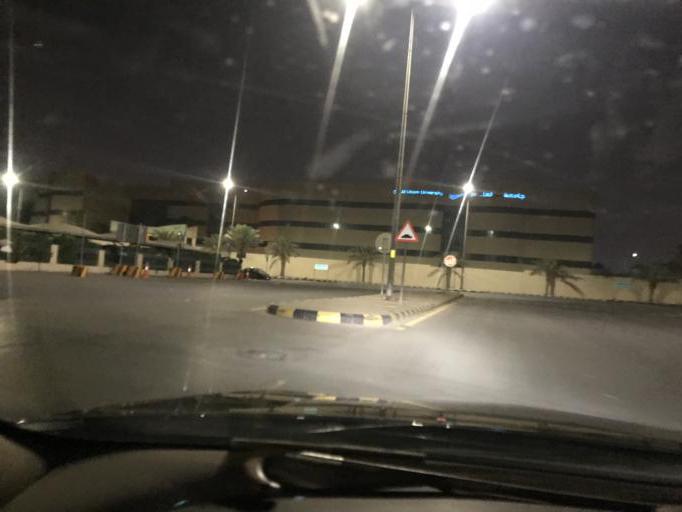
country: SA
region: Ar Riyad
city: Riyadh
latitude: 24.7965
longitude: 46.7099
